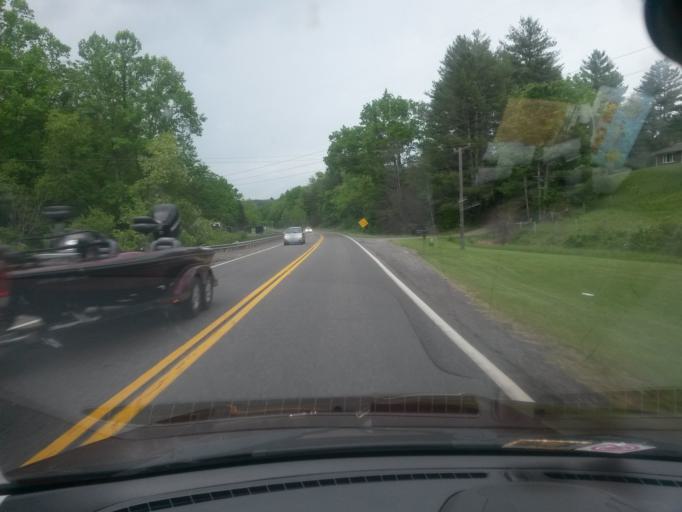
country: US
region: Virginia
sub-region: Floyd County
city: Floyd
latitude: 36.9587
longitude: -80.3683
